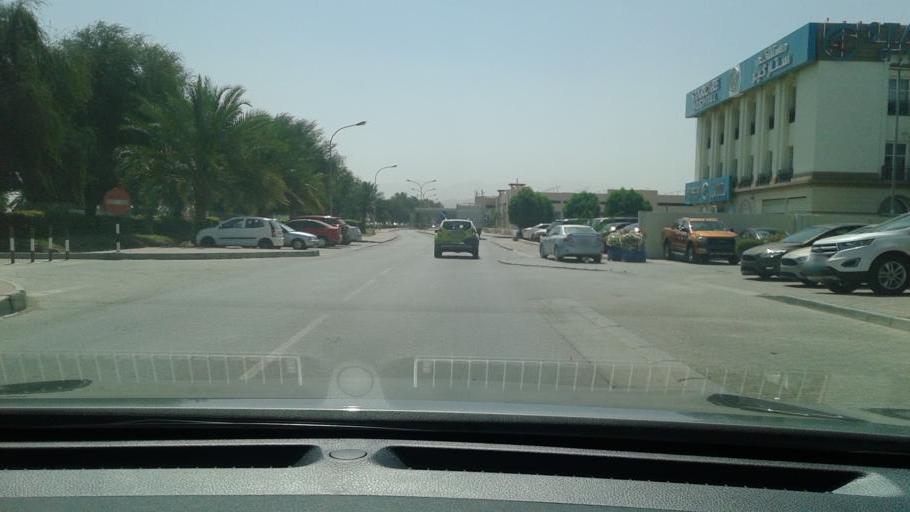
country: OM
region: Muhafazat Masqat
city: As Sib al Jadidah
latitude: 23.6051
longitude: 58.2482
